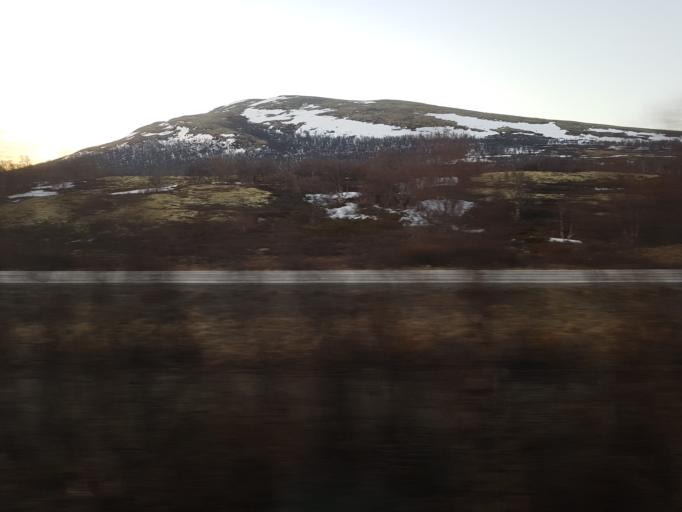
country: NO
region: Sor-Trondelag
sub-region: Oppdal
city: Oppdal
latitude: 62.2534
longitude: 9.5424
